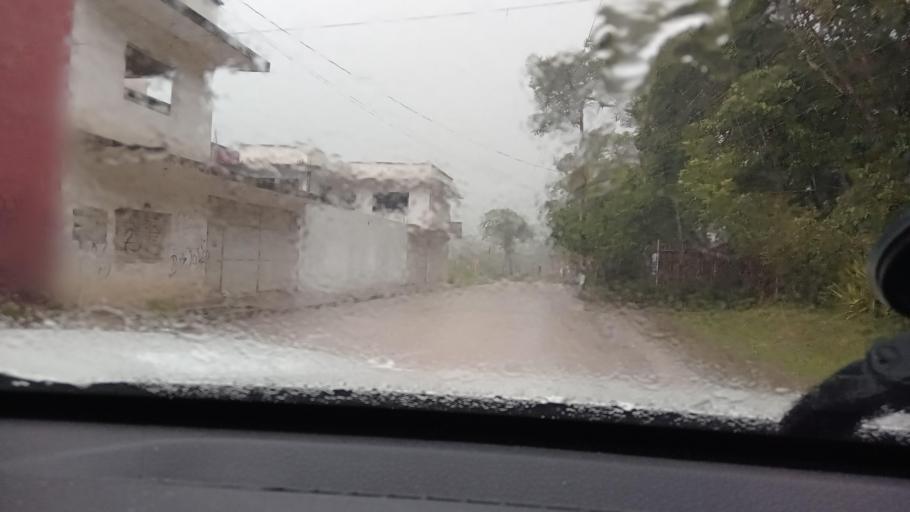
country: MX
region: Veracruz
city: Coatepec
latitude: 19.4586
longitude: -96.9769
